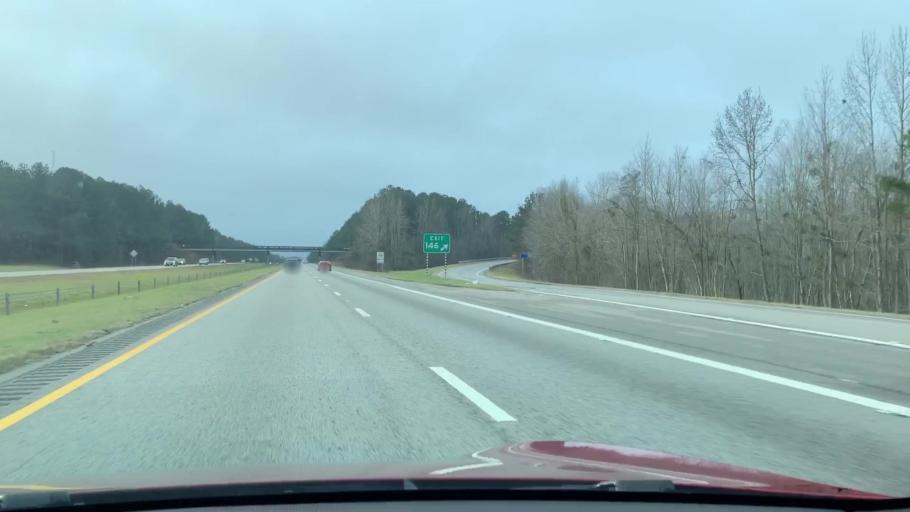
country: US
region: South Carolina
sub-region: Florence County
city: Timmonsville
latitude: 34.0272
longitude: -79.9923
